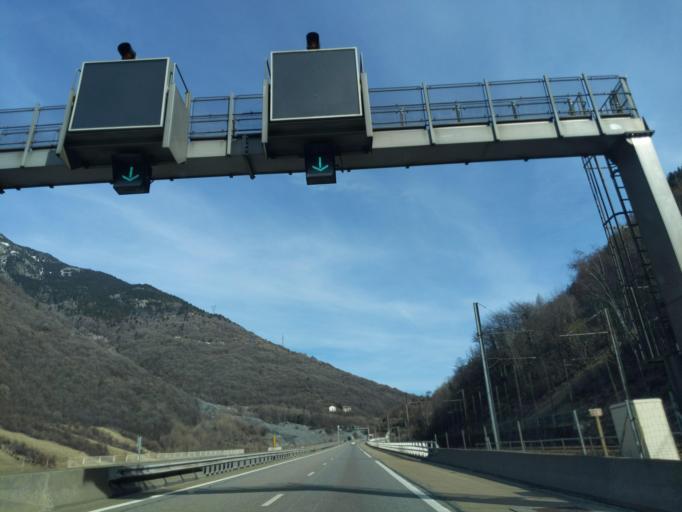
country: FR
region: Rhone-Alpes
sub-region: Departement de la Savoie
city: Saint-Michel-de-Maurienne
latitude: 45.2104
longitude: 6.4996
